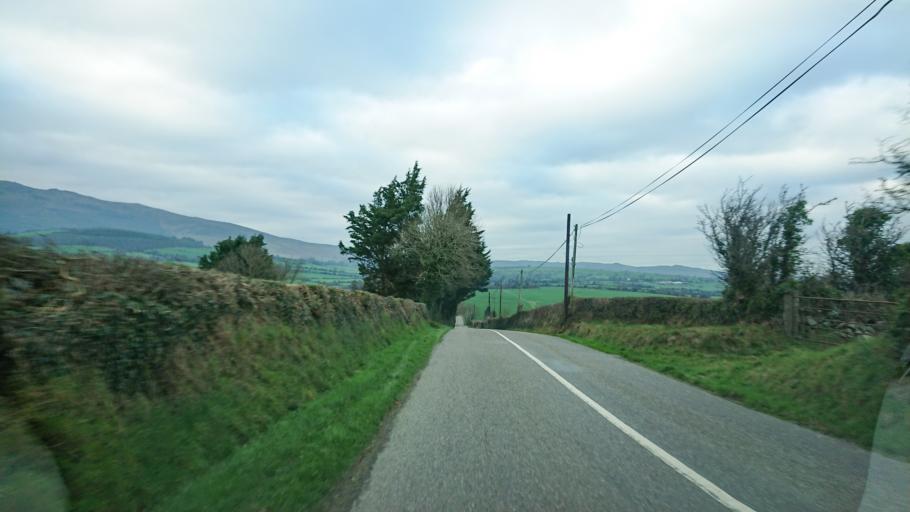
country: IE
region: Munster
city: Carrick-on-Suir
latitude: 52.3131
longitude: -7.5277
